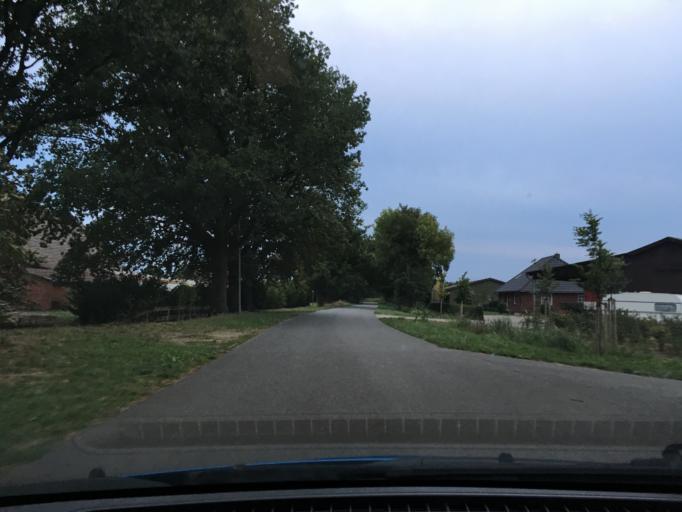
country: DE
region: Lower Saxony
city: Brietlingen
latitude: 53.3493
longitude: 10.4549
